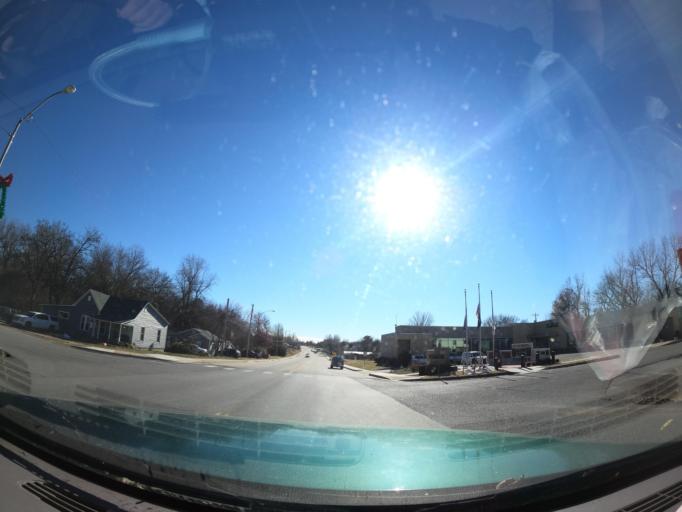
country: US
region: Oklahoma
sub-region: Wagoner County
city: Coweta
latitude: 35.9490
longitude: -95.6506
